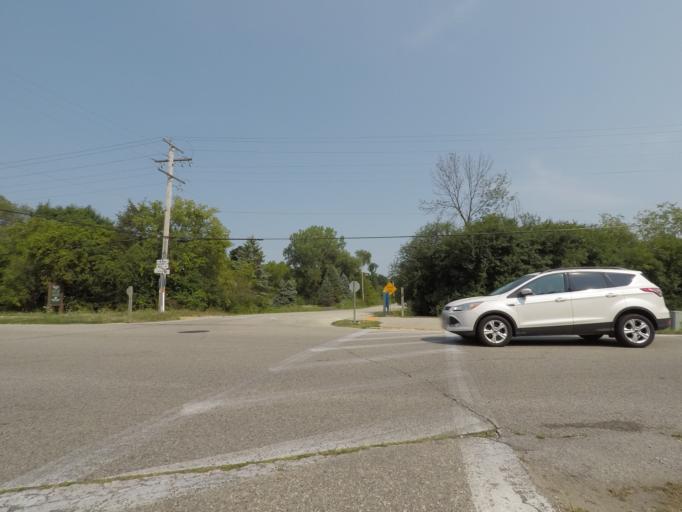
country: US
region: Wisconsin
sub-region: Waukesha County
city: Delafield
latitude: 43.0593
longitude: -88.4140
